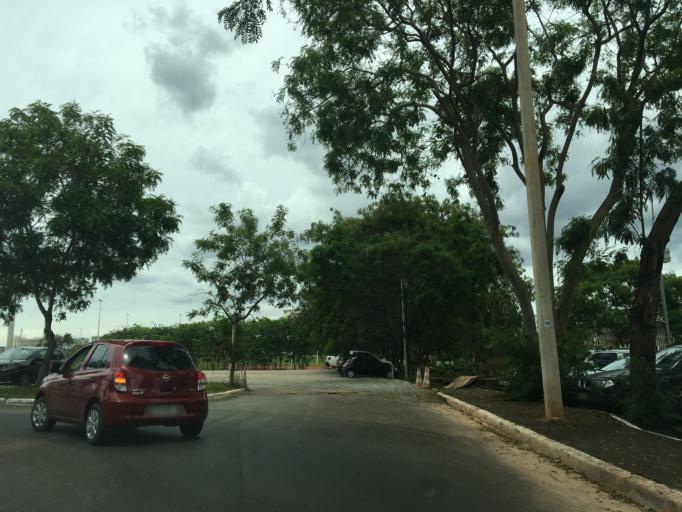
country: BR
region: Federal District
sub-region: Brasilia
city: Brasilia
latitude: -15.7925
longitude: -47.8724
